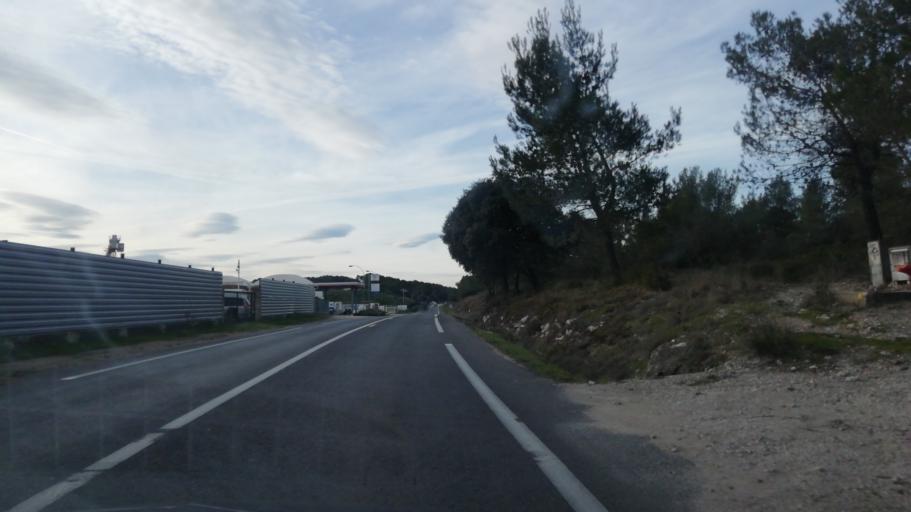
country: FR
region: Languedoc-Roussillon
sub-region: Departement du Gard
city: Caveirac
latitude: 43.8444
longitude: 4.3023
